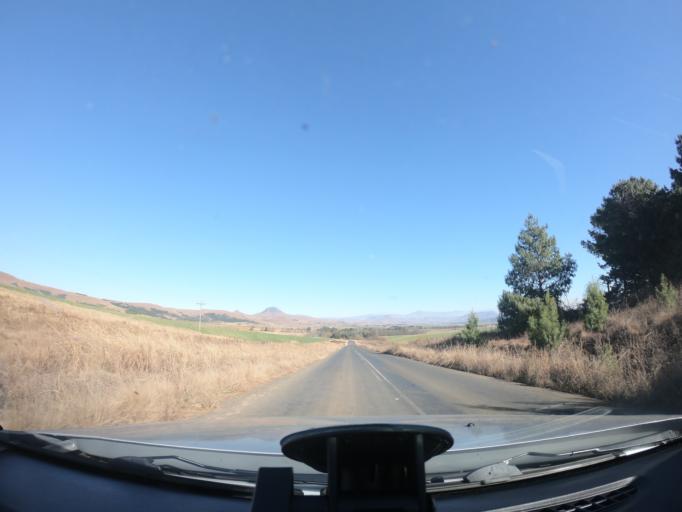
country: ZA
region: KwaZulu-Natal
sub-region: uMgungundlovu District Municipality
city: Mooirivier
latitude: -29.3261
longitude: 29.8547
